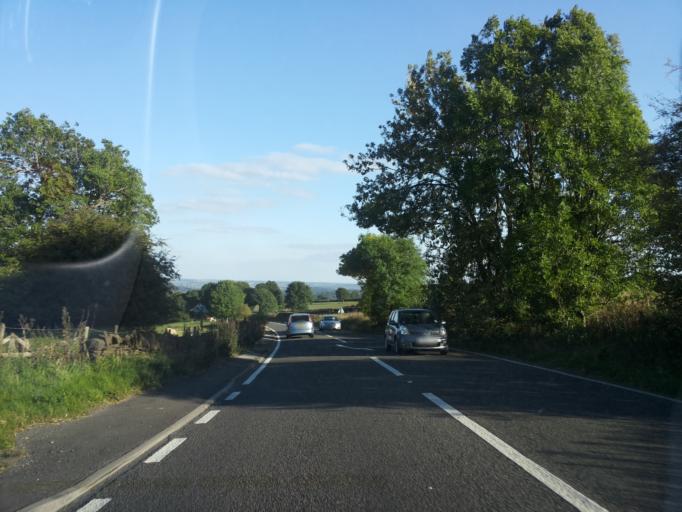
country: GB
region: England
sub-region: Derbyshire
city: Dronfield
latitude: 53.2334
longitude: -1.5301
